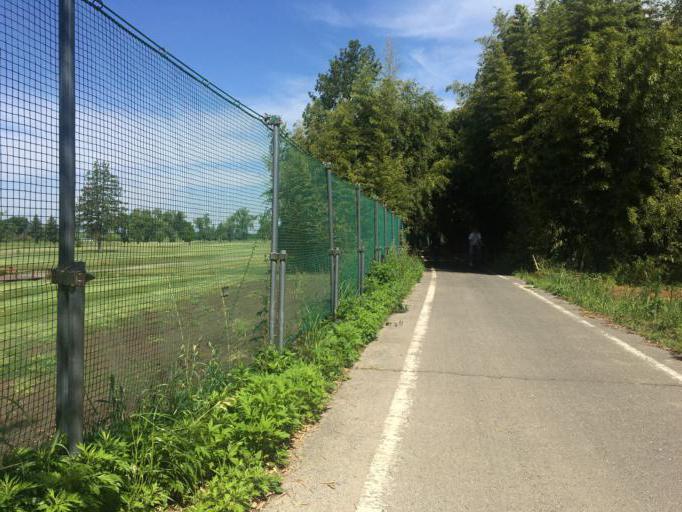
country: JP
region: Saitama
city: Shiki
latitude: 35.8622
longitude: 139.5865
